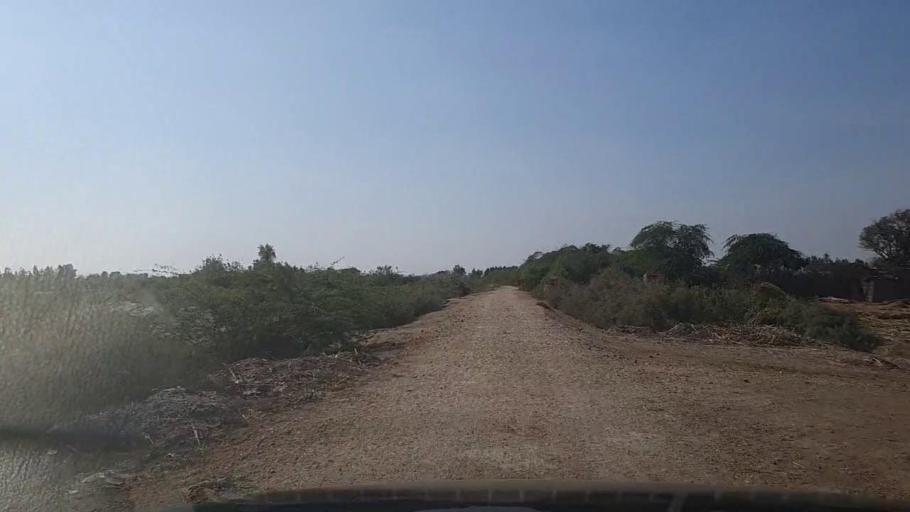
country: PK
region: Sindh
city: Gharo
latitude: 24.7075
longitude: 67.7417
